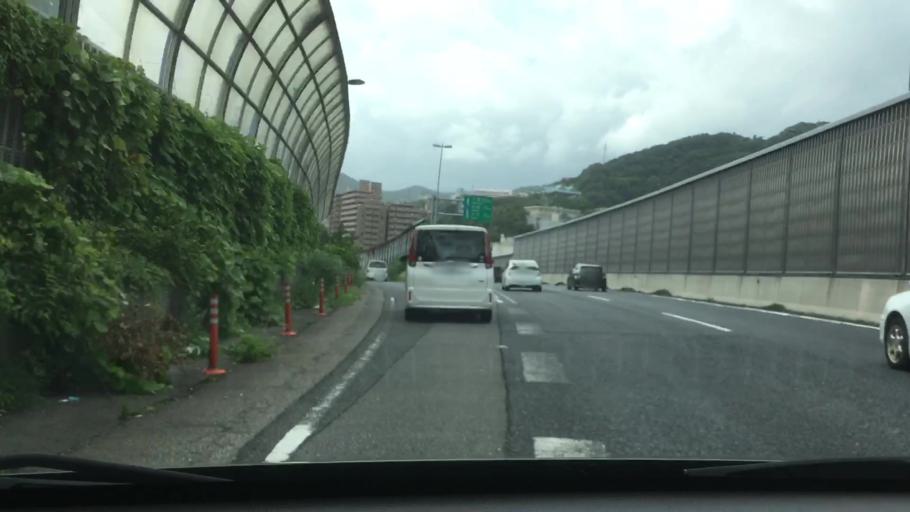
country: JP
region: Hiroshima
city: Hiroshima-shi
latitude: 34.3945
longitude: 132.4164
